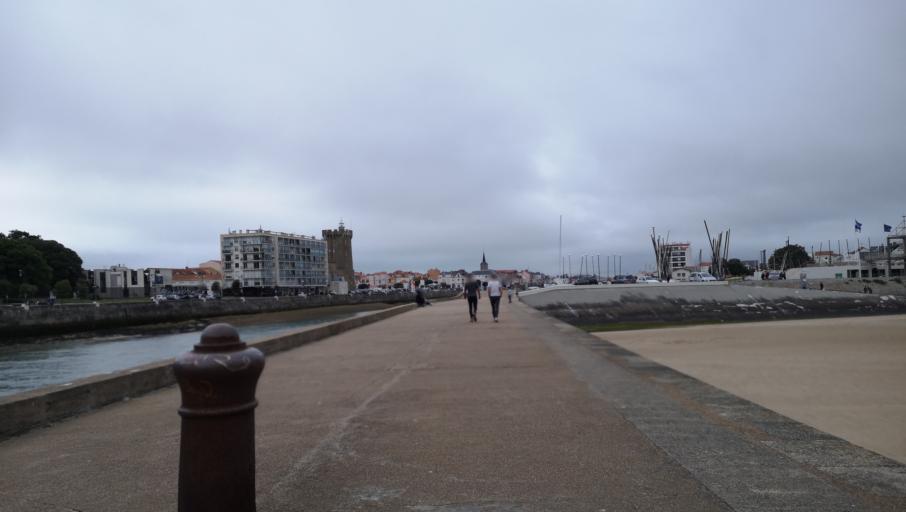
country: FR
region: Pays de la Loire
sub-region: Departement de la Vendee
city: Les Sables-d'Olonne
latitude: 46.4918
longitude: -1.7929
